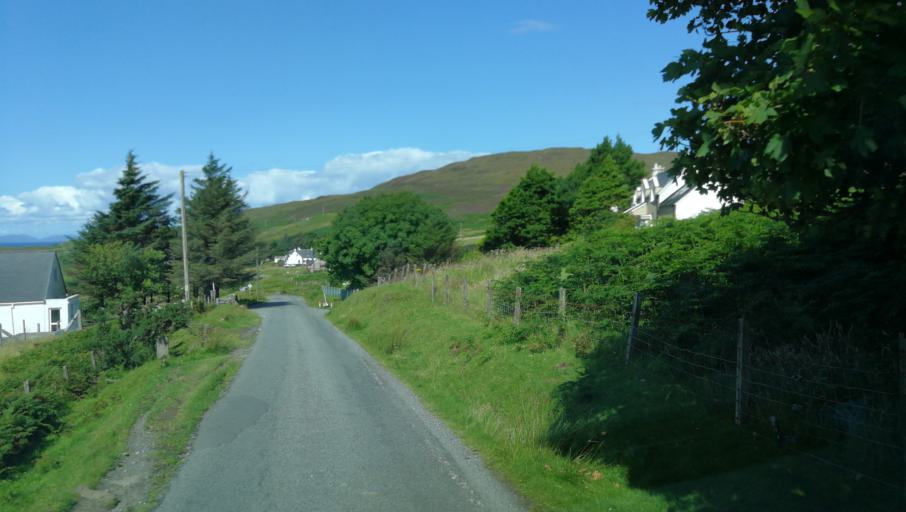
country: GB
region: Scotland
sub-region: Highland
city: Isle of Skye
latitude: 57.4494
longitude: -6.6929
